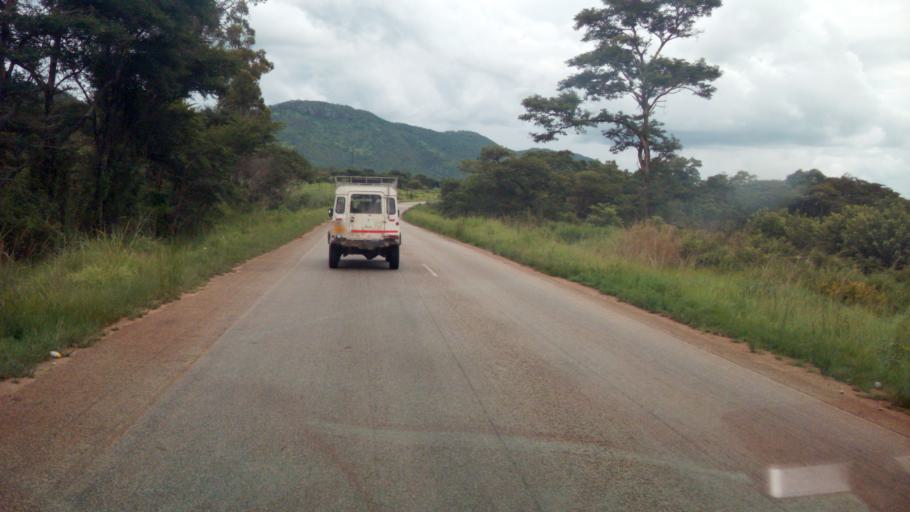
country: ZW
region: Mashonaland Central
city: Mazowe
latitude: -17.5930
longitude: 30.9645
